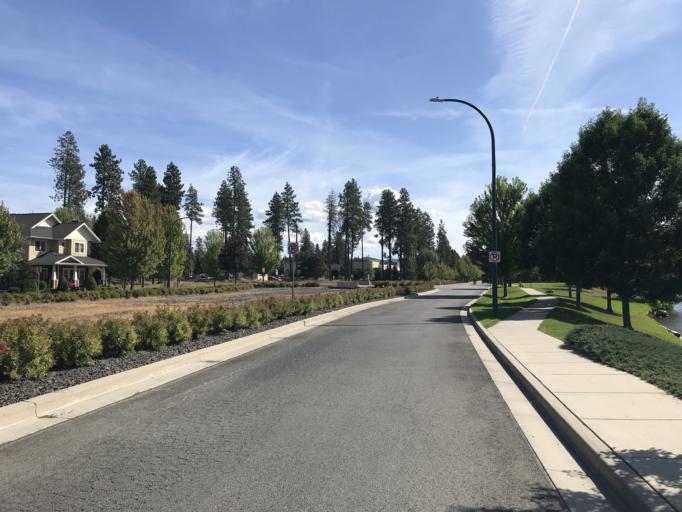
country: US
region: Idaho
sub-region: Kootenai County
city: Coeur d'Alene
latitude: 47.7006
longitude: -116.8415
